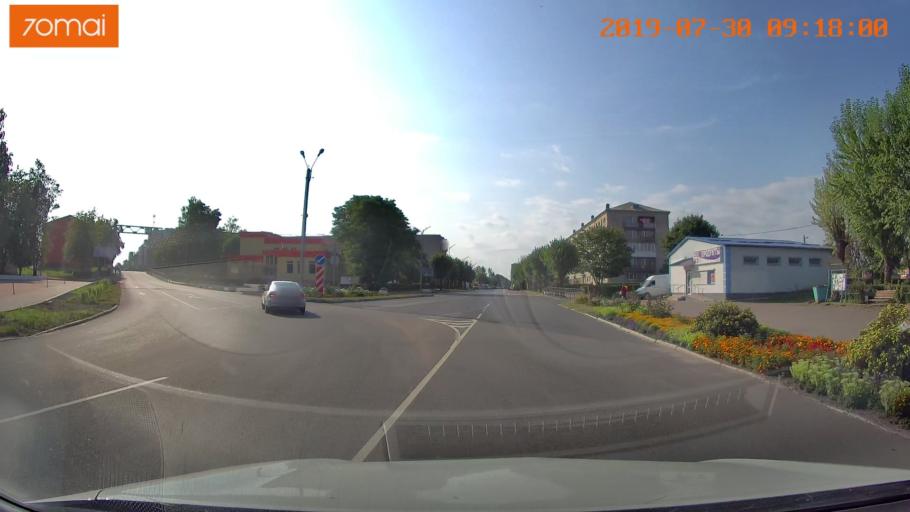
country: RU
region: Kaliningrad
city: Nesterov
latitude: 54.6314
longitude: 22.5719
